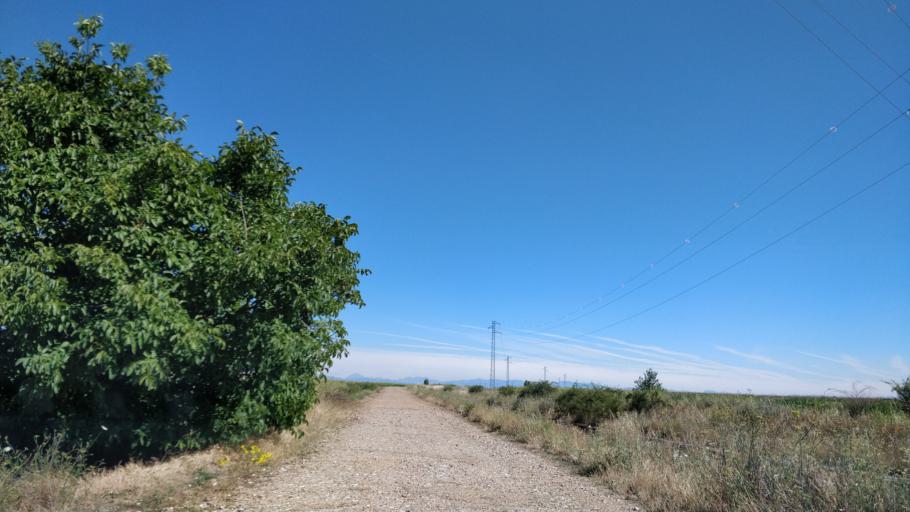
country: ES
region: Castille and Leon
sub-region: Provincia de Leon
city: Bustillo del Paramo
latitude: 42.4295
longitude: -5.8218
